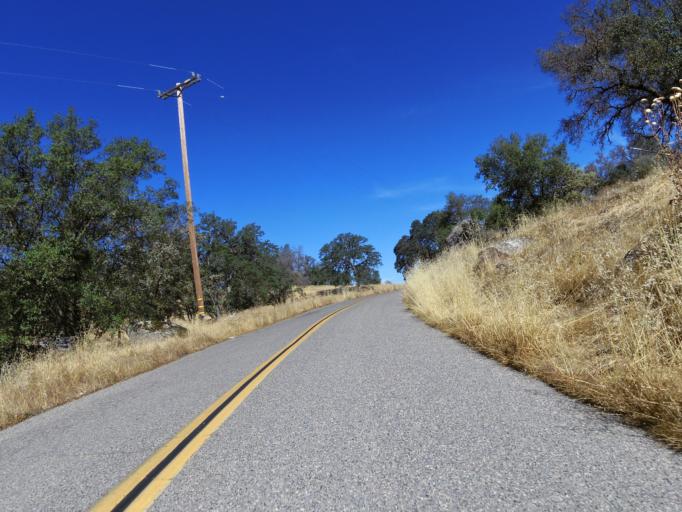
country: US
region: California
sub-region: Madera County
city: Yosemite Lakes
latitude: 37.2579
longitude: -119.9563
